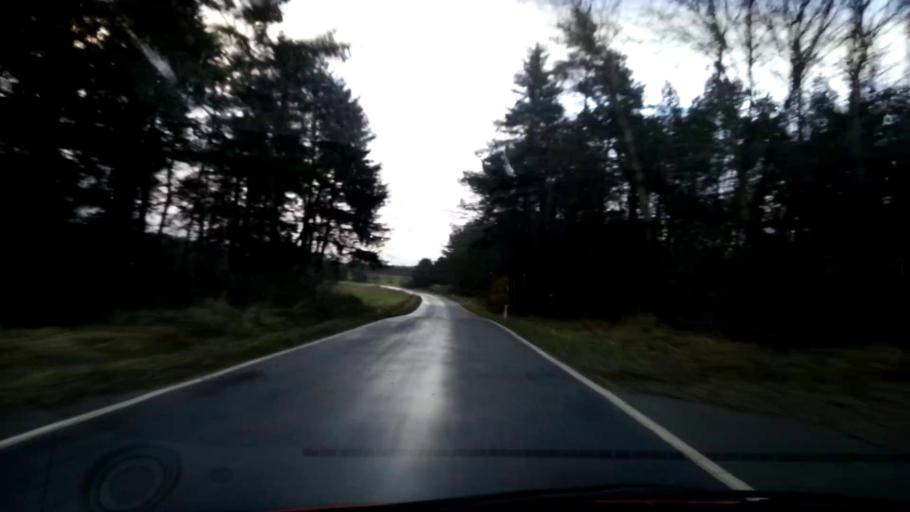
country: DE
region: Bavaria
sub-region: Upper Franconia
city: Konigsfeld
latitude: 49.9261
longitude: 11.1900
